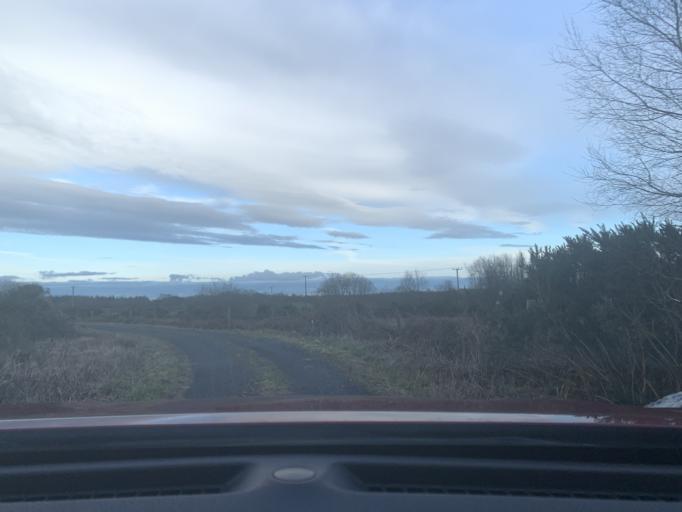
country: IE
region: Connaught
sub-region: Roscommon
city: Ballaghaderreen
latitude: 53.8874
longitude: -8.5743
